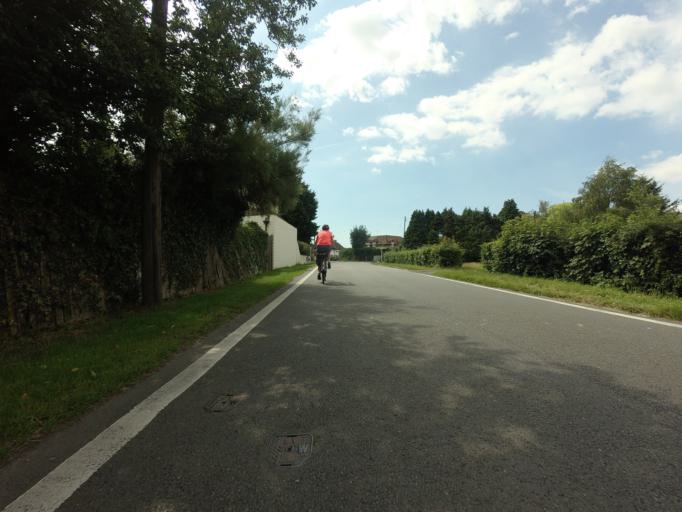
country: GB
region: England
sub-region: Kent
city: Stone
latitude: 51.0423
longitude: 0.7849
